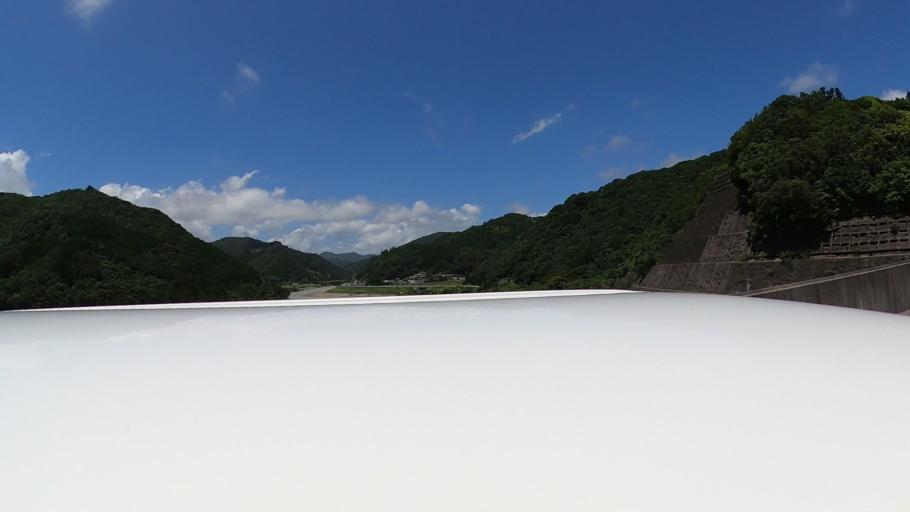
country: JP
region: Miyazaki
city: Takanabe
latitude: 32.3440
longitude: 131.5994
